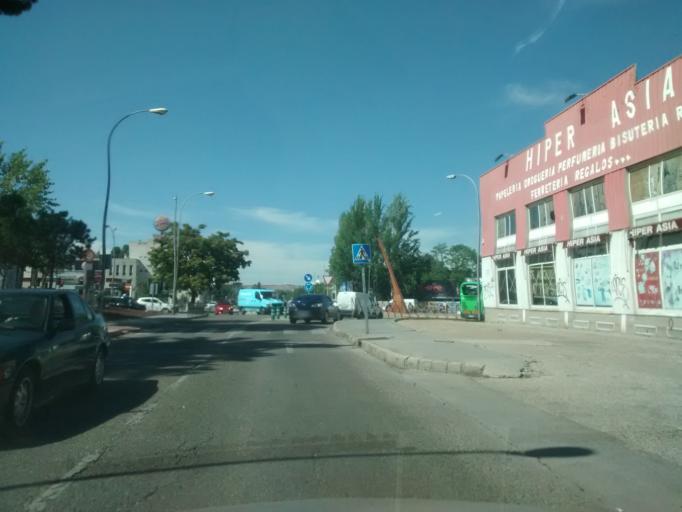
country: ES
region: Madrid
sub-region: Provincia de Madrid
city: San Fernando de Henares
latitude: 40.4318
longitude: -3.5333
